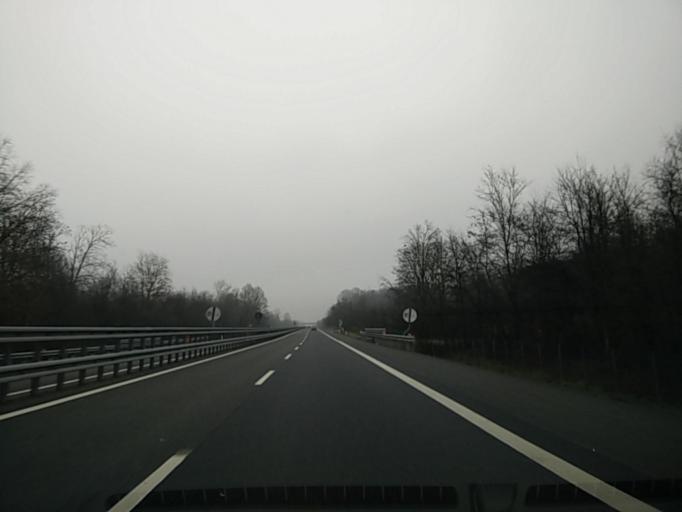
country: IT
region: Piedmont
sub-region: Provincia di Asti
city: Dusino
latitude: 44.9357
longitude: 7.9924
